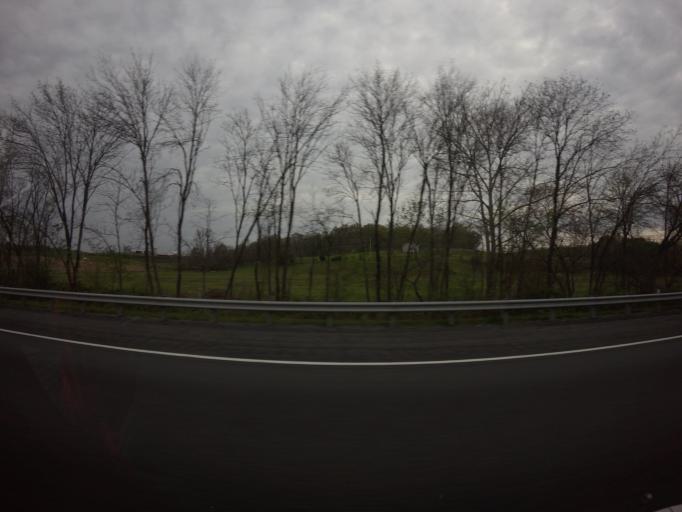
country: US
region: Maryland
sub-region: Carroll County
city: Mount Airy
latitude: 39.3700
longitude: -77.2134
